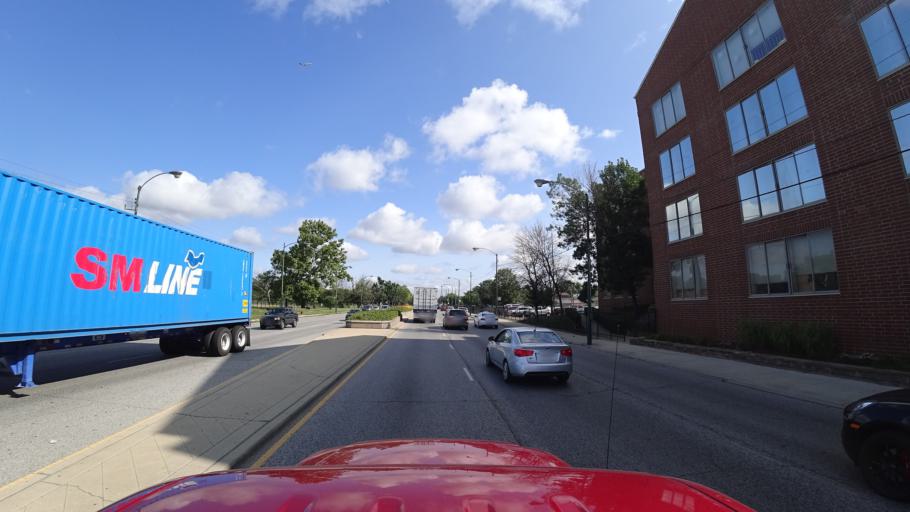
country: US
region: Illinois
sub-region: Cook County
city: Cicero
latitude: 41.8116
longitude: -87.7432
